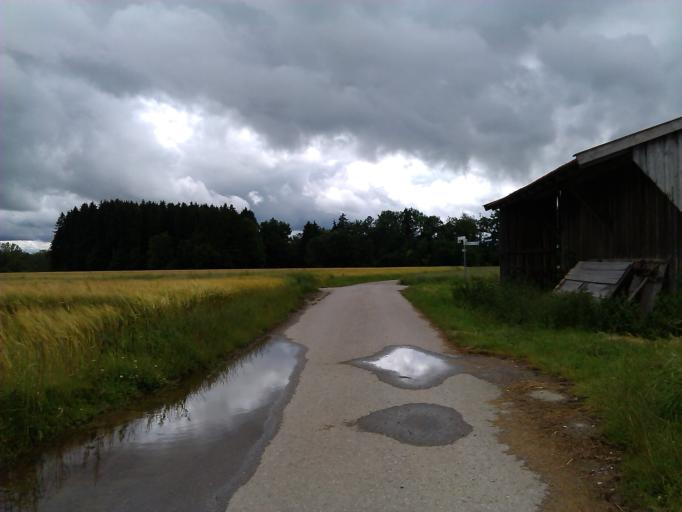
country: DE
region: Bavaria
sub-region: Swabia
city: Pforzen
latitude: 47.9532
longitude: 10.6208
